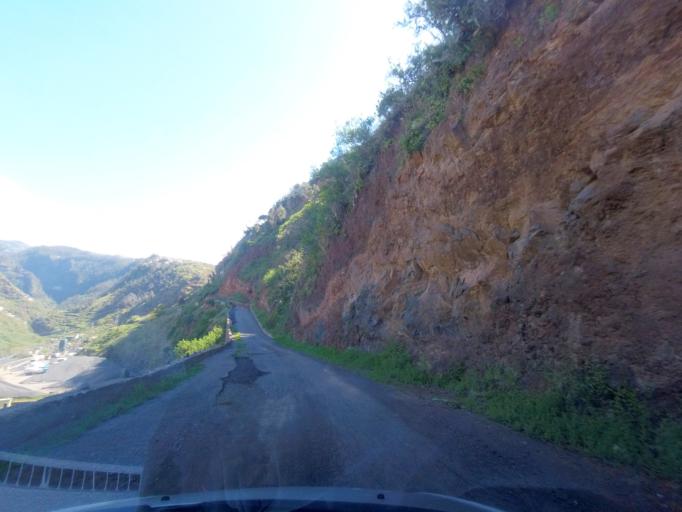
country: PT
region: Madeira
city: Camara de Lobos
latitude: 32.6570
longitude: -16.9622
